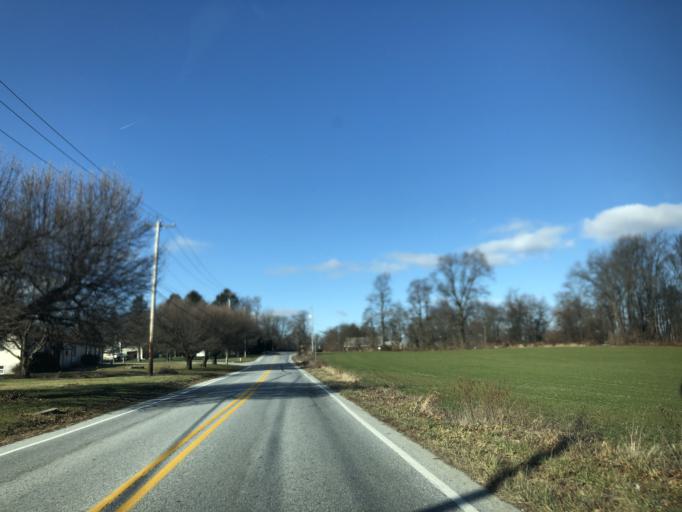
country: US
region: Pennsylvania
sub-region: Chester County
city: Coatesville
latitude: 39.9864
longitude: -75.8705
